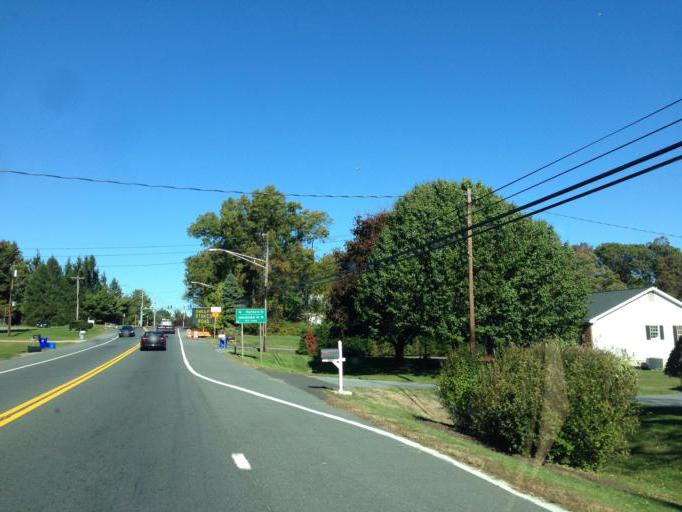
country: US
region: Maryland
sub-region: Montgomery County
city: Damascus
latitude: 39.2604
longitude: -77.2230
